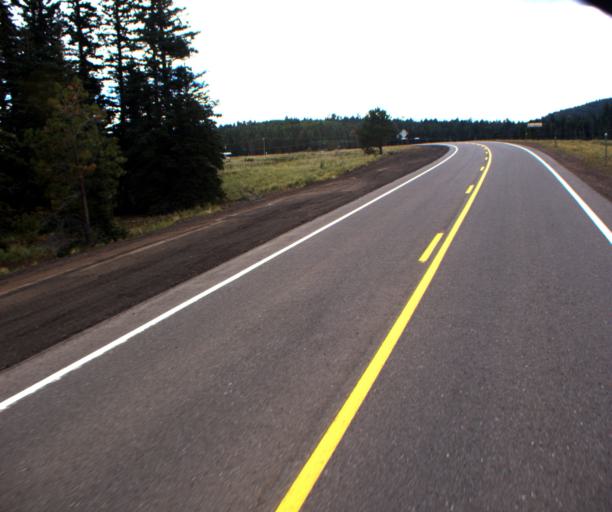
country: US
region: Arizona
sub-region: Apache County
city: Eagar
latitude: 34.0018
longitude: -109.5580
